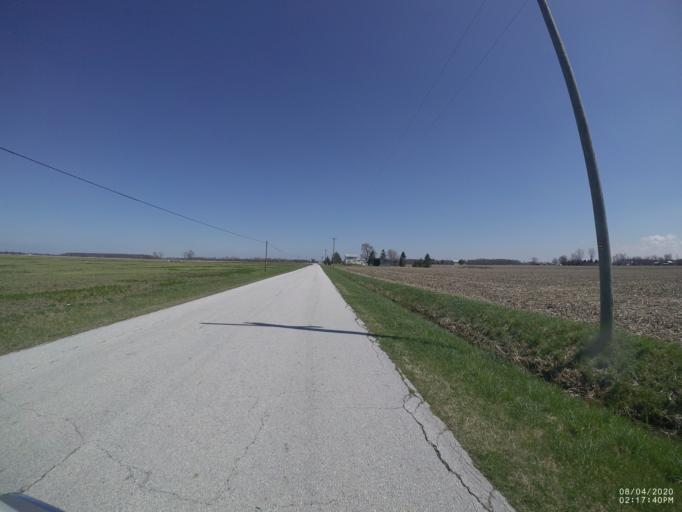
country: US
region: Ohio
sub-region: Sandusky County
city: Stony Prairie
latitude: 41.2821
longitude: -83.2402
